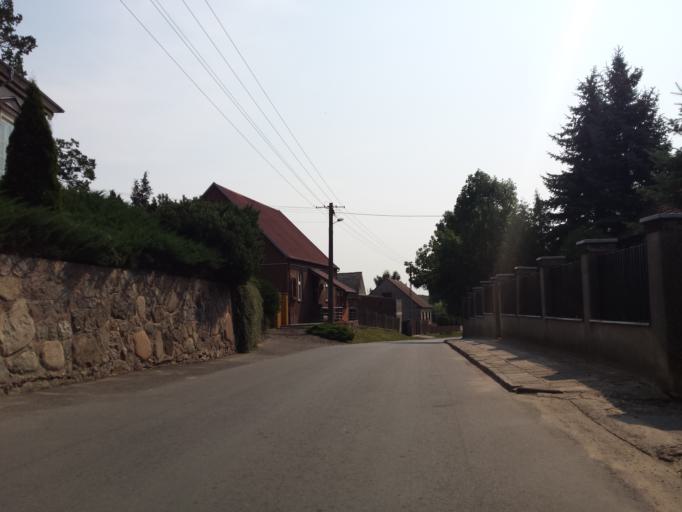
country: PL
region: Greater Poland Voivodeship
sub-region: Powiat czarnkowsko-trzcianecki
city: Polajewo
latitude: 52.7734
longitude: 16.6426
